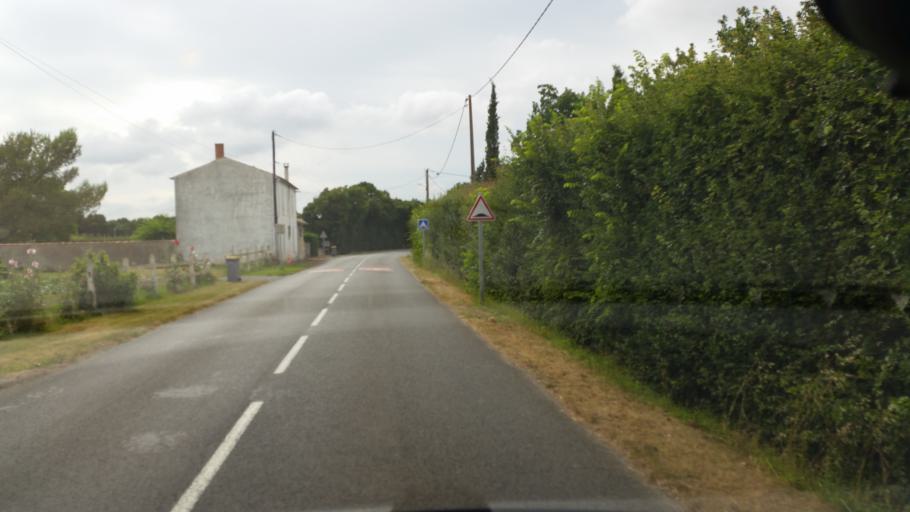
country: FR
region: Poitou-Charentes
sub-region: Departement de la Charente-Maritime
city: Saint-Jean-de-Liversay
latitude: 46.2136
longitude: -0.8799
